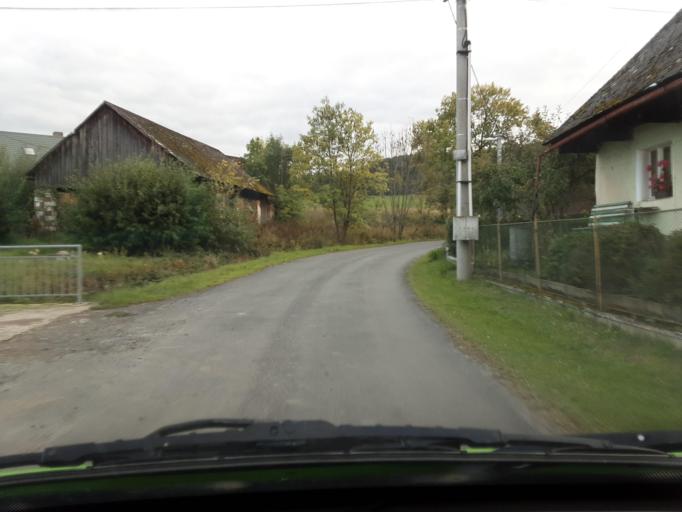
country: CZ
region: Plzensky
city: Janovice nad Uhlavou
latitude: 49.3867
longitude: 13.1505
